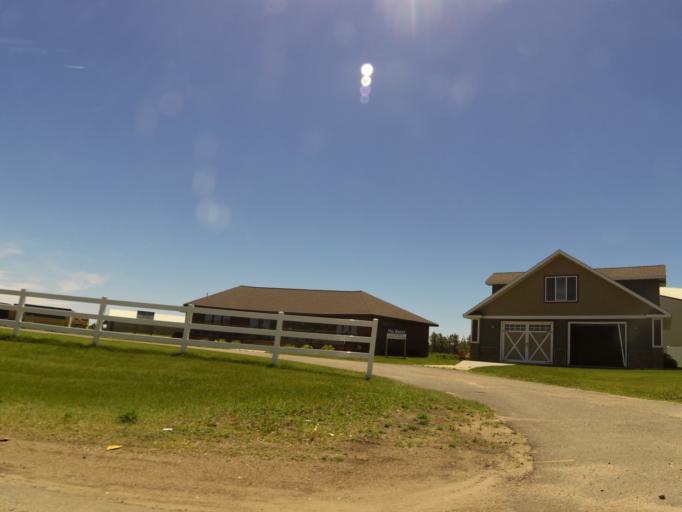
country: US
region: Minnesota
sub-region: Wadena County
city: Wadena
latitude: 46.4468
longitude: -95.1488
